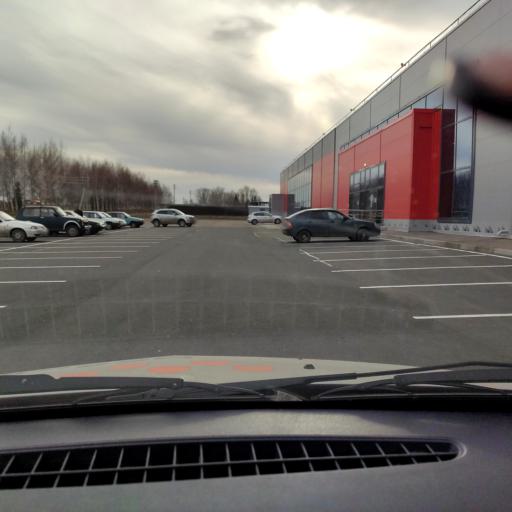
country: RU
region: Bashkortostan
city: Ufa
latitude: 54.6164
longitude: 55.9250
